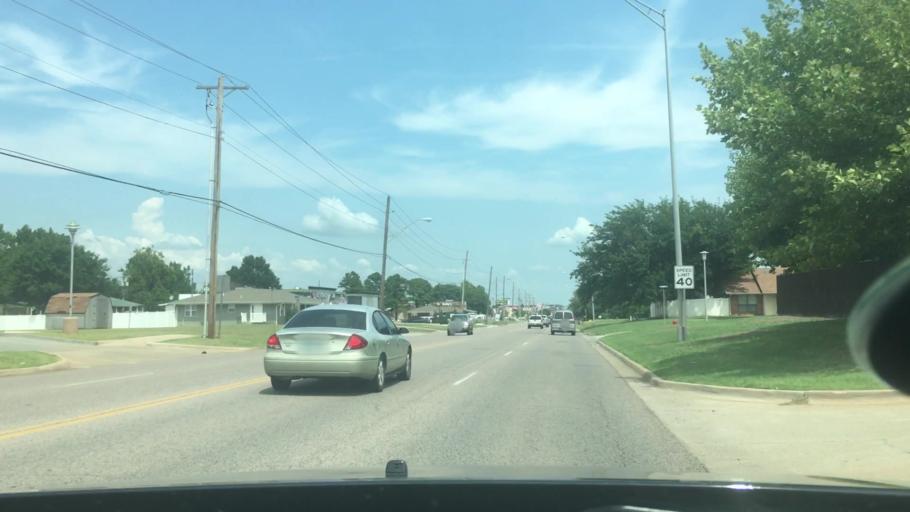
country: US
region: Oklahoma
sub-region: Pottawatomie County
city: Shawnee
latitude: 35.3717
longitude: -96.9297
